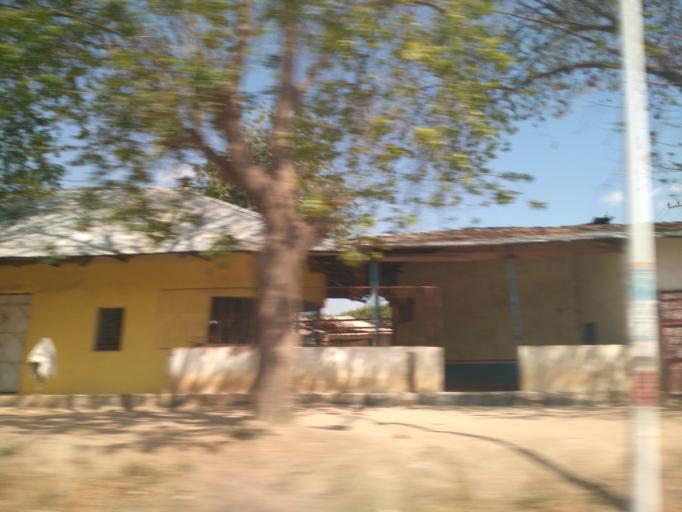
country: TZ
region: Dodoma
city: Dodoma
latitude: -6.1611
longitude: 35.7208
